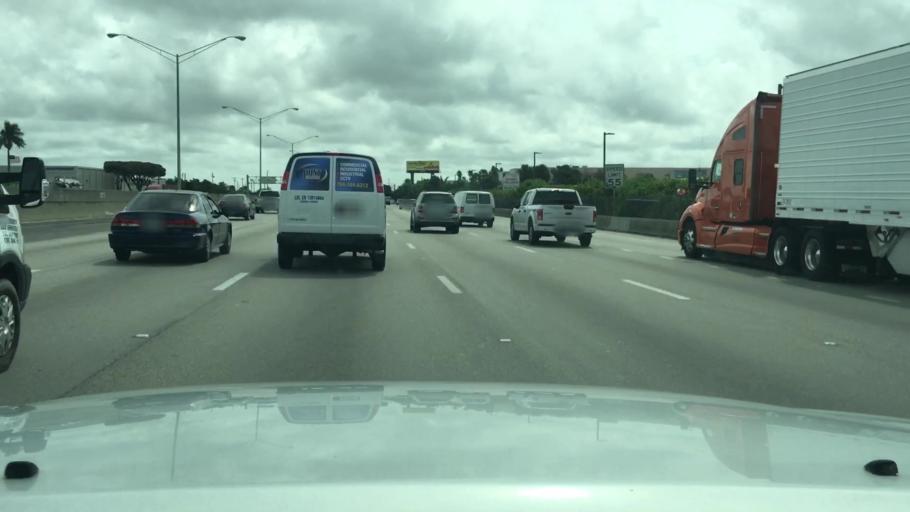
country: US
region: Florida
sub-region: Miami-Dade County
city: Virginia Gardens
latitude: 25.8183
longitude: -80.3220
